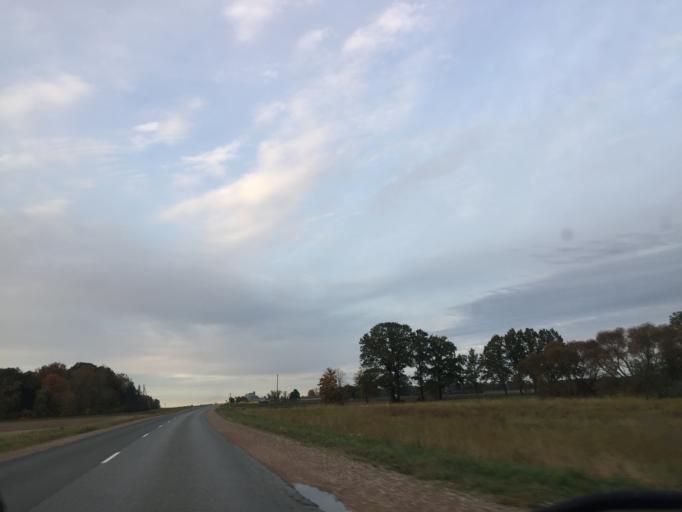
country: LV
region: Dobeles Rajons
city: Dobele
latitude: 56.7117
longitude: 23.3820
